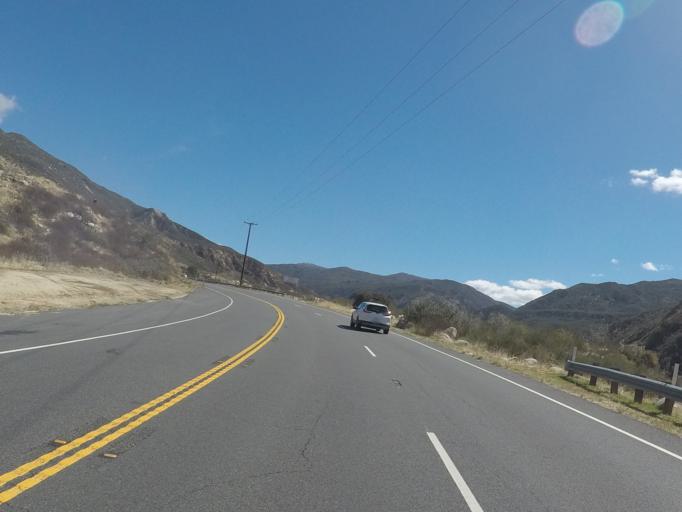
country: US
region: California
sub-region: Riverside County
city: Idyllwild-Pine Cove
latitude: 33.7213
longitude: -116.8003
